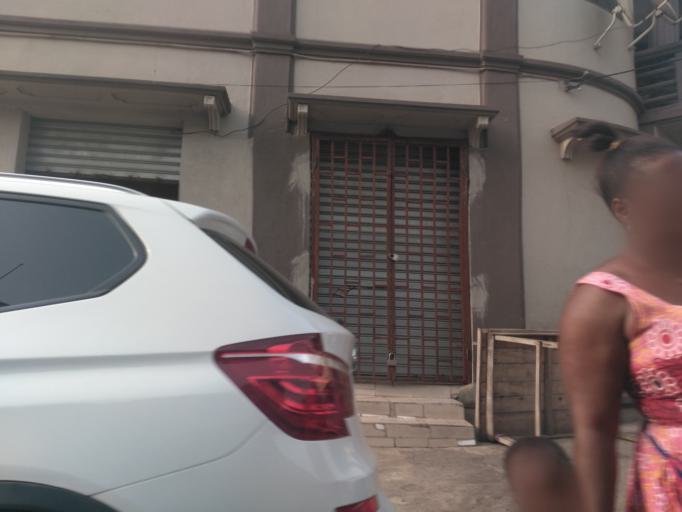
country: GH
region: Ashanti
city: Kumasi
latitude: 6.6881
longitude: -1.6134
